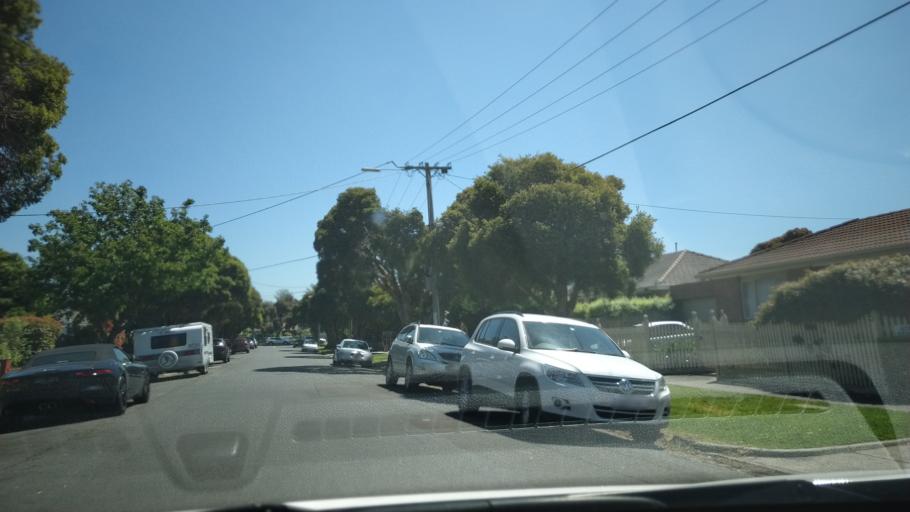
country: AU
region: Victoria
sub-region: Glen Eira
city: Glen Huntly
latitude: -37.8931
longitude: 145.0434
